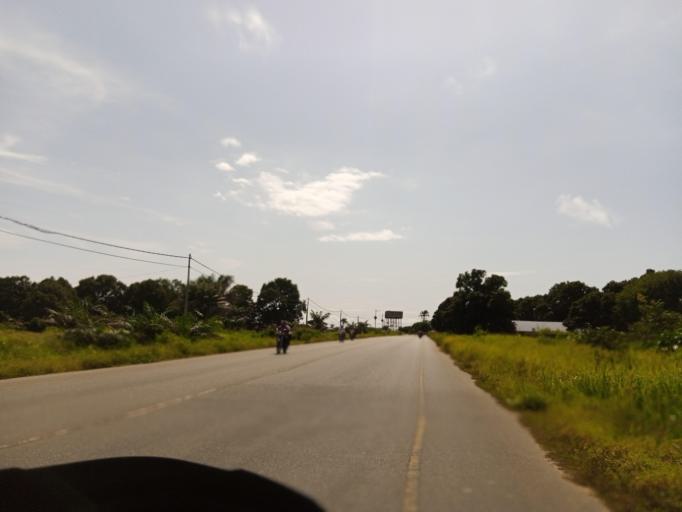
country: SL
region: Northern Province
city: Tintafor
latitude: 8.6171
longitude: -13.2080
